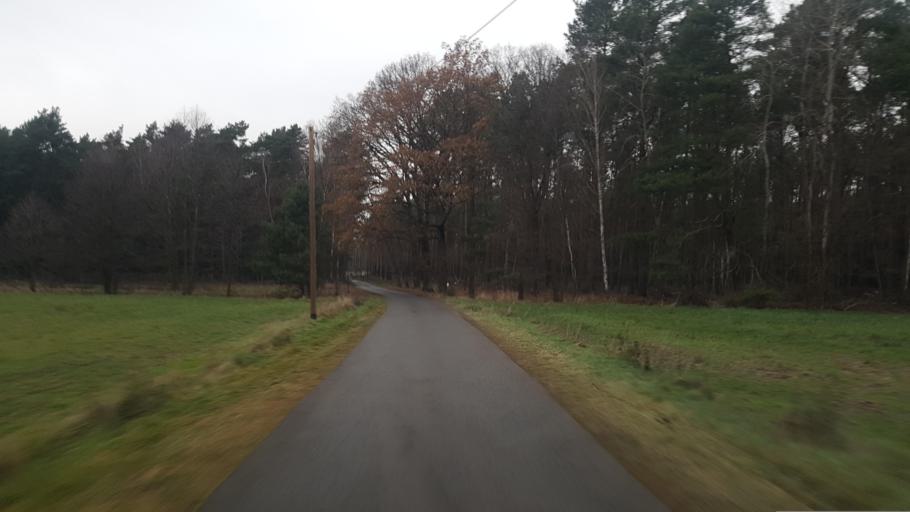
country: DE
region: Brandenburg
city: Cottbus
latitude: 51.6840
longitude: 14.3319
